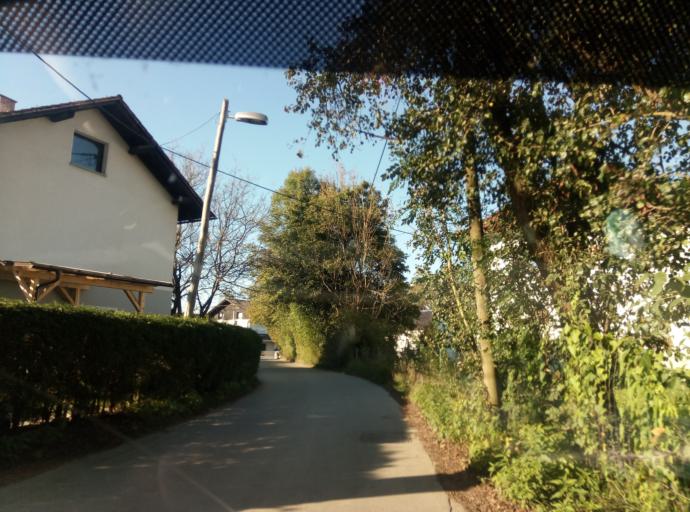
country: SI
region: Ljubljana
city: Ljubljana
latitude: 46.0976
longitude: 14.5029
